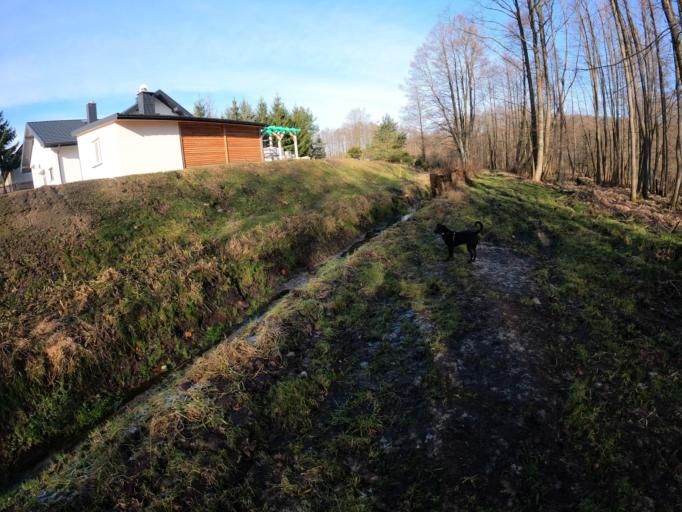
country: PL
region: West Pomeranian Voivodeship
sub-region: Powiat koszalinski
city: Polanow
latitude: 54.1167
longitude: 16.6904
